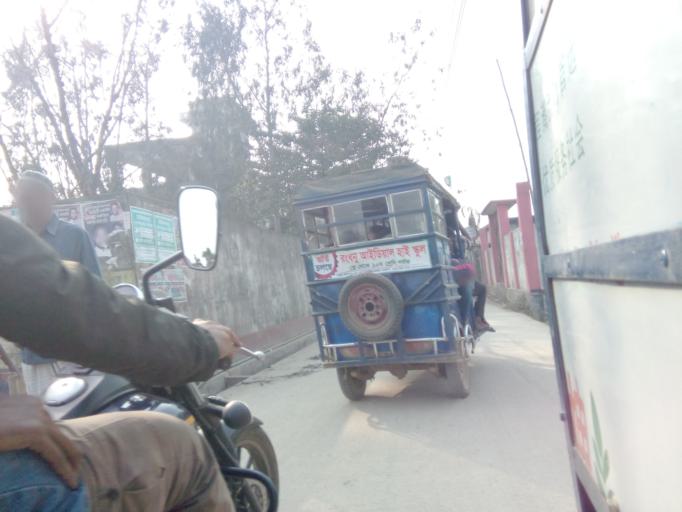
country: BD
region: Dhaka
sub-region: Dhaka
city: Dhaka
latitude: 23.7039
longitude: 90.4760
